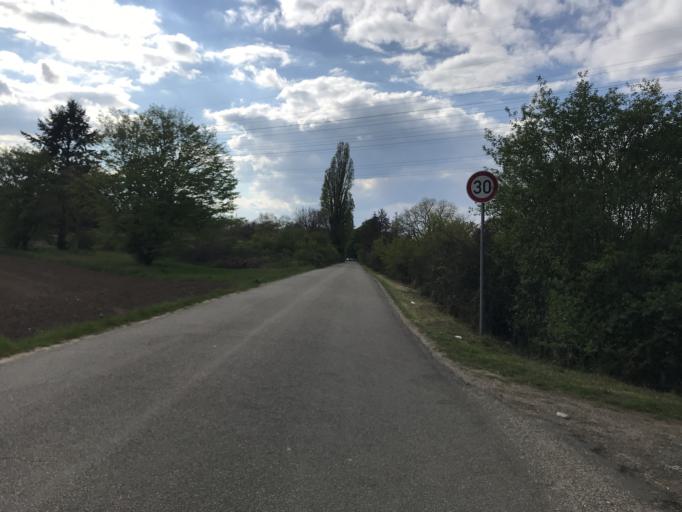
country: DE
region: Hesse
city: Kelsterbach
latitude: 50.0960
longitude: 8.5551
